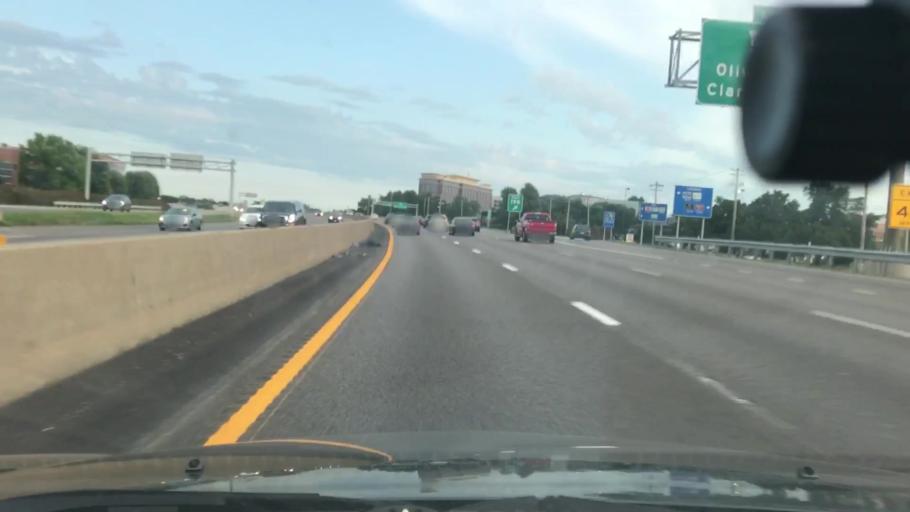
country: US
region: Missouri
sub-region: Saint Louis County
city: Chesterfield
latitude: 38.6568
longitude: -90.5650
